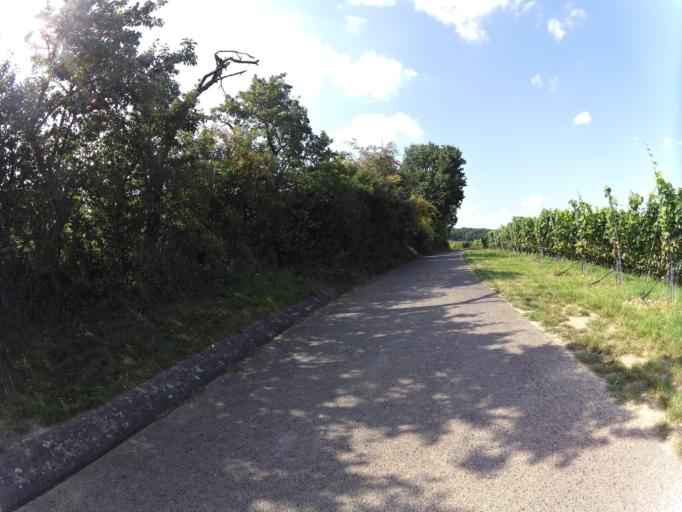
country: DE
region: Bavaria
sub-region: Regierungsbezirk Unterfranken
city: Nordheim
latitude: 49.8365
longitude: 10.1724
